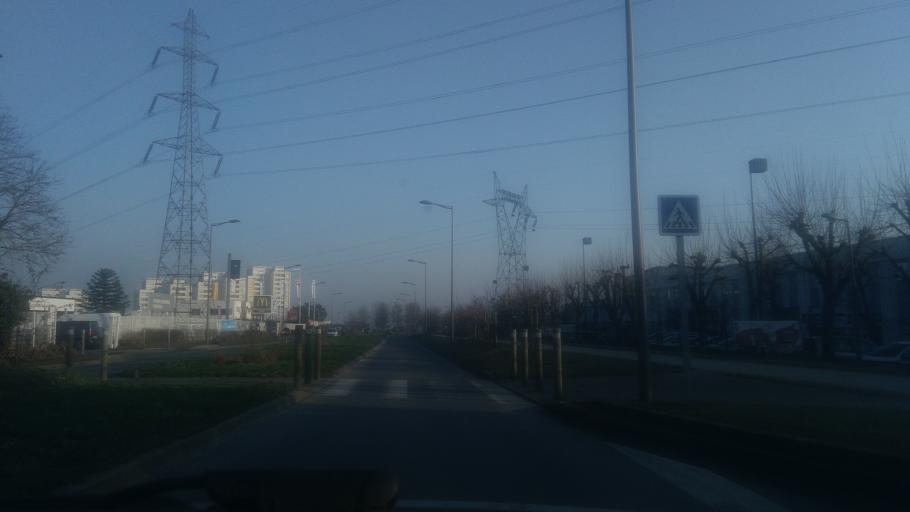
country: FR
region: Ile-de-France
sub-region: Departement du Val-d'Oise
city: Osny
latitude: 49.0506
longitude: 2.0715
